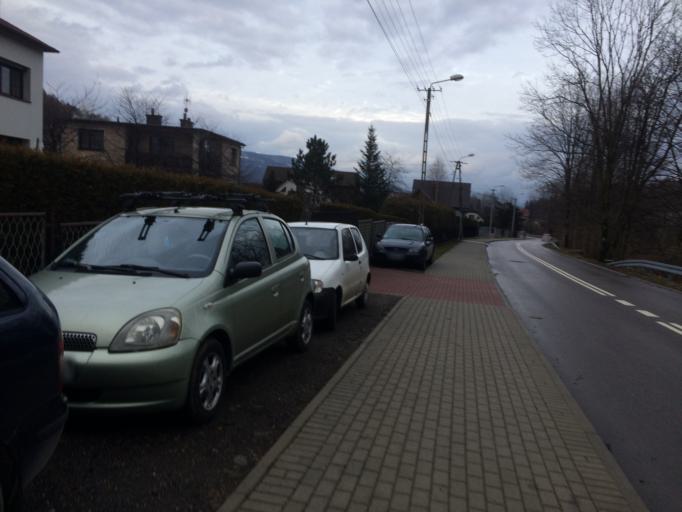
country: PL
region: Silesian Voivodeship
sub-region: Powiat bielski
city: Bystra
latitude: 49.7603
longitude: 19.0407
